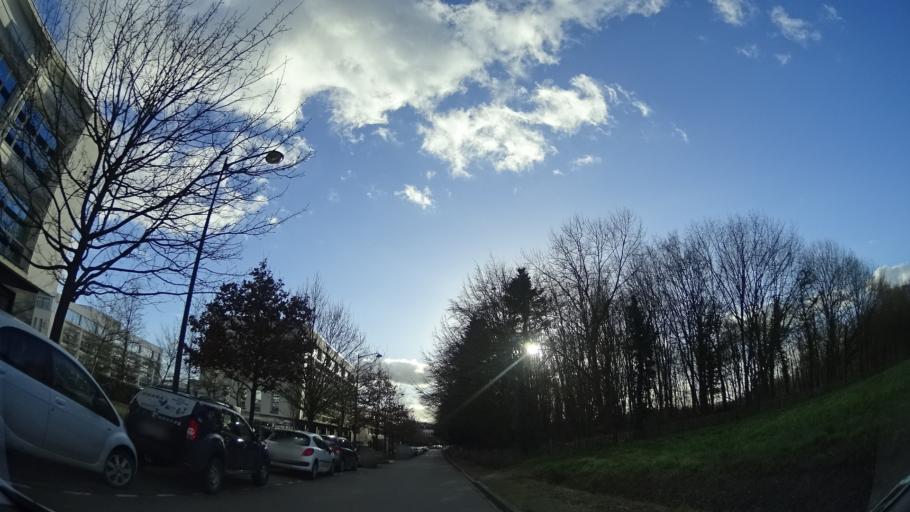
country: FR
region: Brittany
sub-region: Departement d'Ille-et-Vilaine
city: Cesson-Sevigne
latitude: 48.1337
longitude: -1.6385
